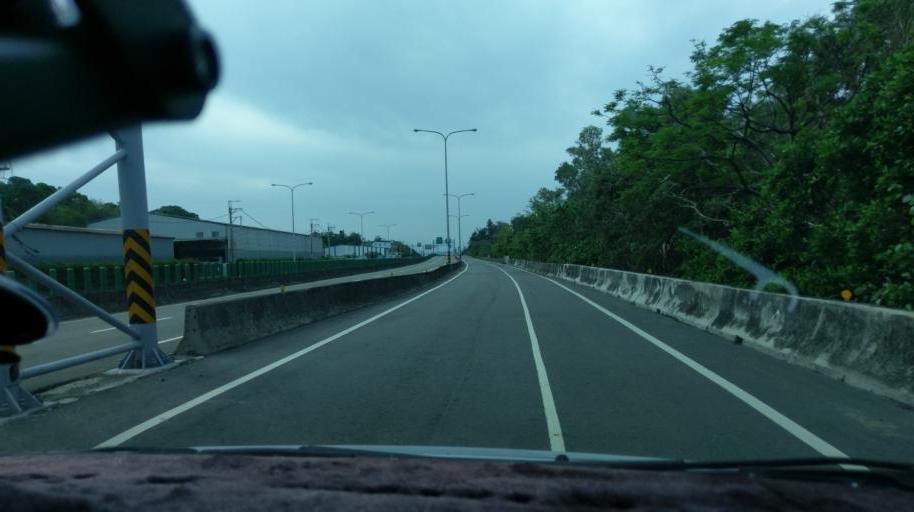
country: TW
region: Taiwan
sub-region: Hsinchu
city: Hsinchu
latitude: 24.7209
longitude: 120.8682
